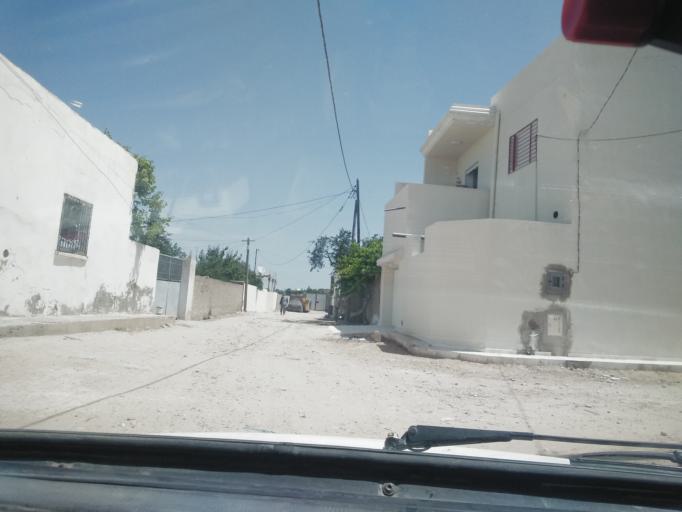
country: TN
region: Safaqis
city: Al Qarmadah
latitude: 34.8086
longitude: 10.7739
